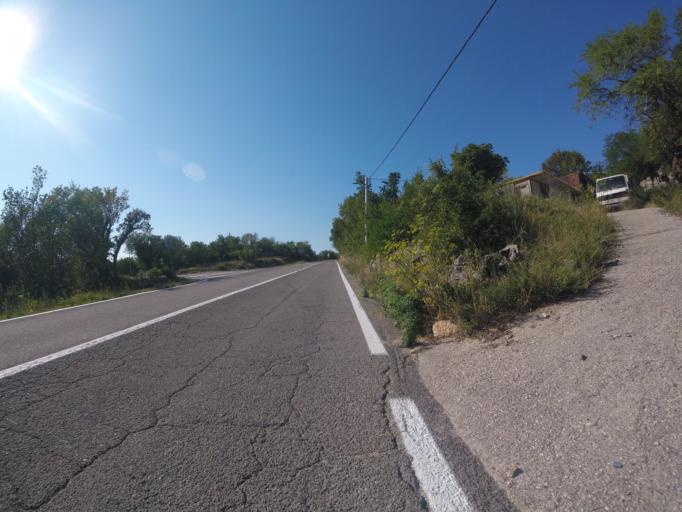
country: HR
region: Primorsko-Goranska
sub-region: Grad Crikvenica
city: Jadranovo
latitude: 45.2492
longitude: 14.6081
